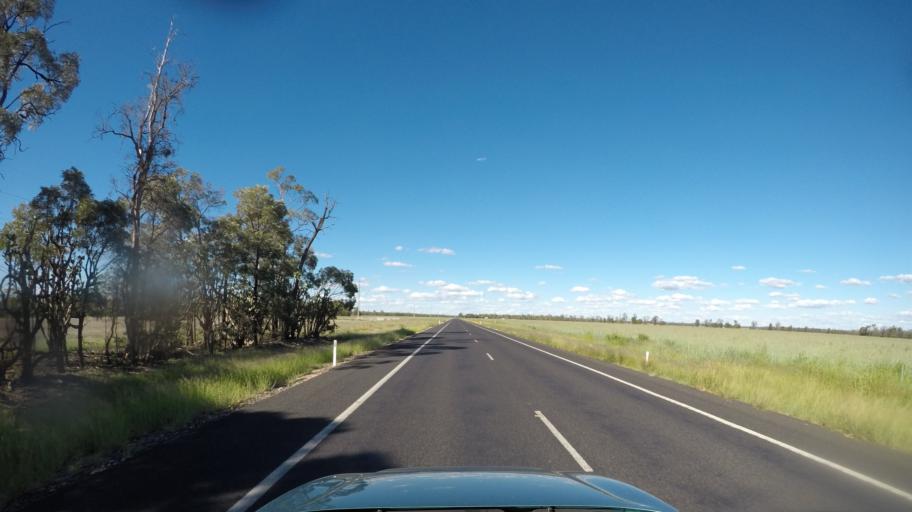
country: AU
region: Queensland
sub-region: Goondiwindi
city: Goondiwindi
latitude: -28.1279
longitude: 150.7023
